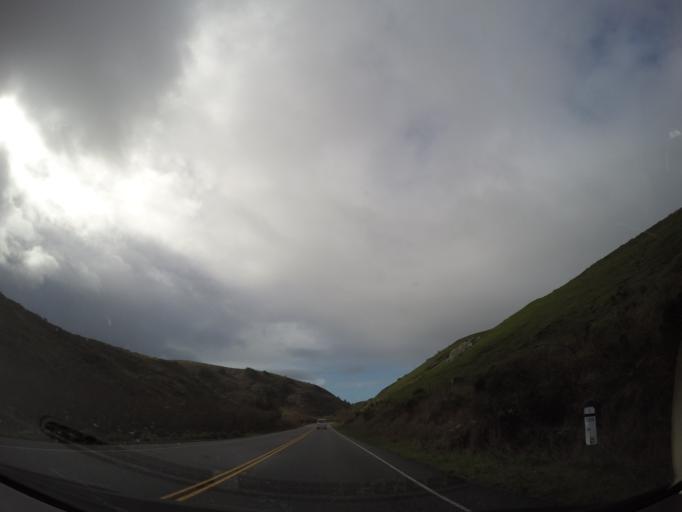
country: US
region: California
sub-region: Sonoma County
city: Bodega Bay
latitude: 38.3275
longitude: -123.0001
